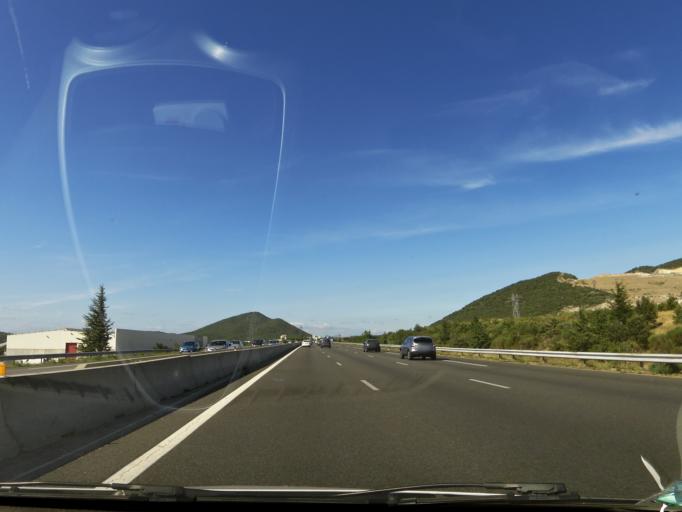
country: FR
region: Rhone-Alpes
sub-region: Departement de la Drome
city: Malataverne
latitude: 44.4475
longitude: 4.7538
